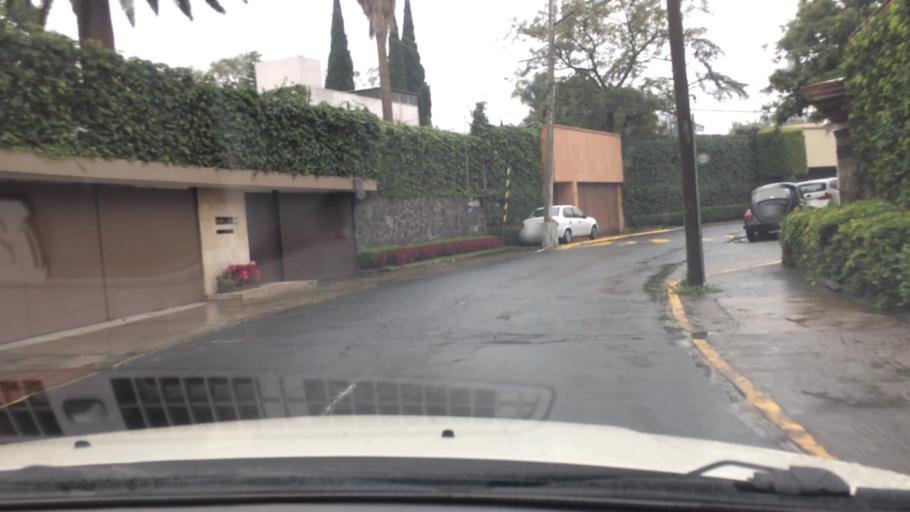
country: MX
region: Mexico City
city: Magdalena Contreras
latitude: 19.3283
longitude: -99.2012
